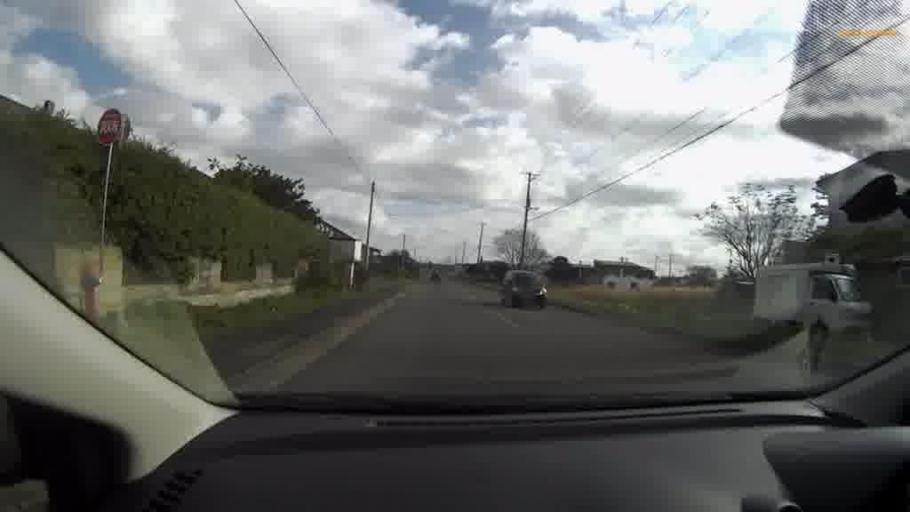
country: JP
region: Hokkaido
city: Kushiro
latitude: 42.9758
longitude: 144.1223
